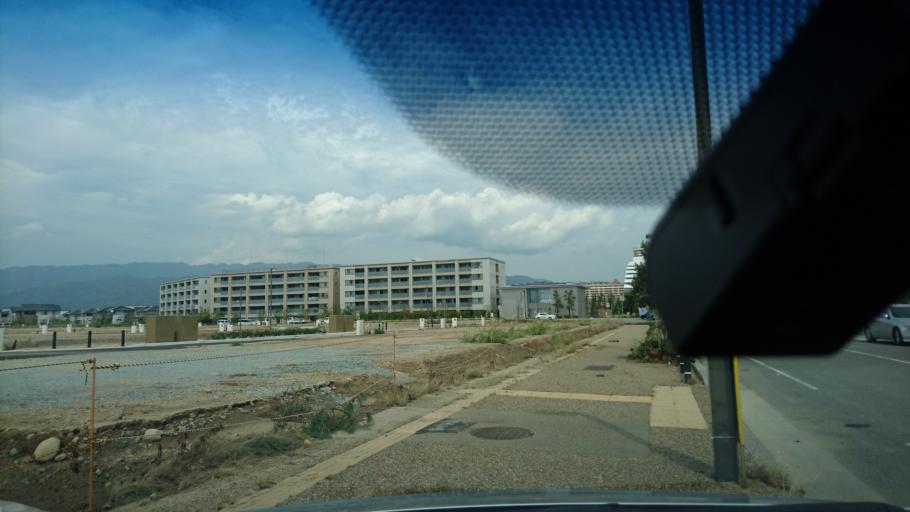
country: JP
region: Hyogo
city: Nishinomiya-hama
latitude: 34.7065
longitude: 135.3215
